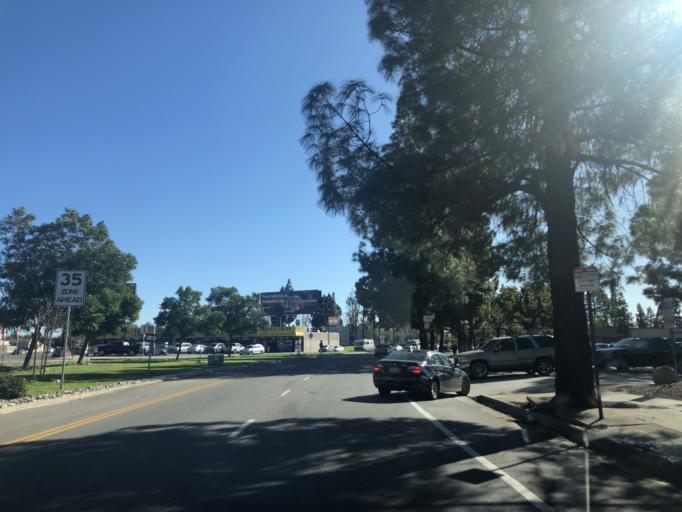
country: US
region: California
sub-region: Los Angeles County
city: North Hollywood
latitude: 34.2251
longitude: -118.3968
